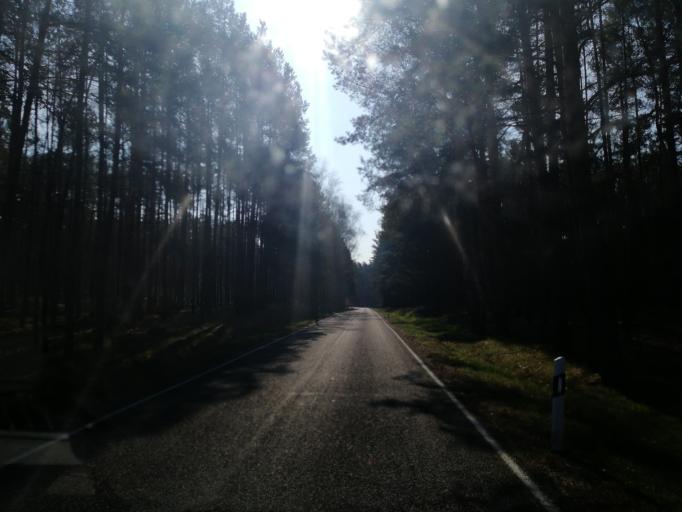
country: DE
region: Brandenburg
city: Sonnewalde
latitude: 51.7738
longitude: 13.6388
